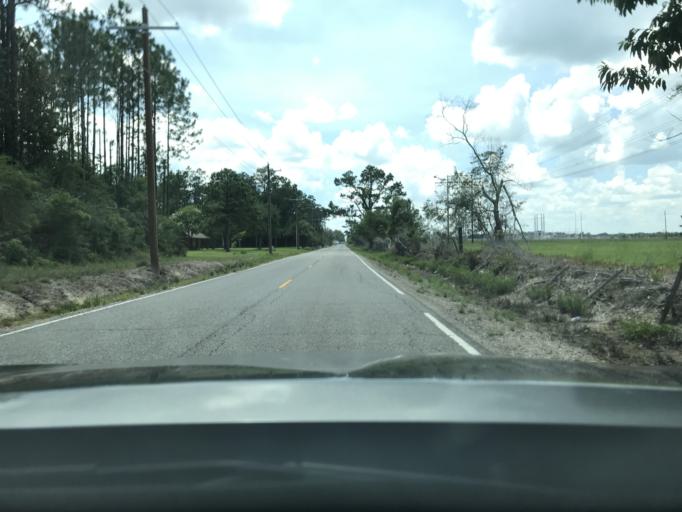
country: US
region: Louisiana
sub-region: Calcasieu Parish
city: Moss Bluff
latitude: 30.3300
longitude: -93.1628
